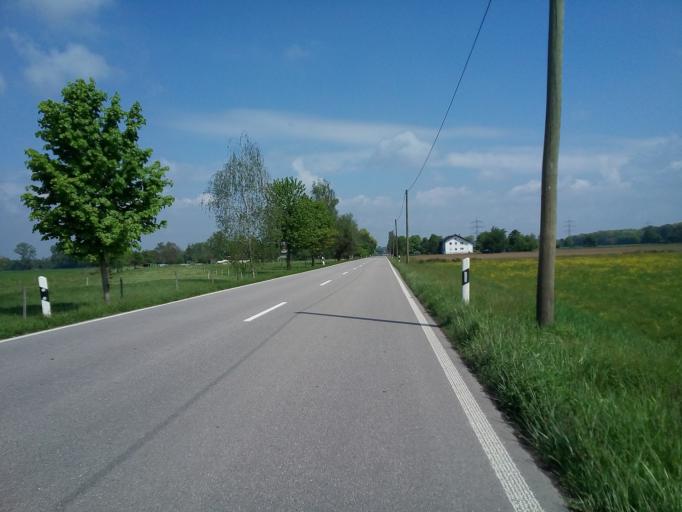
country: DE
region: Baden-Wuerttemberg
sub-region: Freiburg Region
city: Rheinau
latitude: 48.6577
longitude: 7.9929
